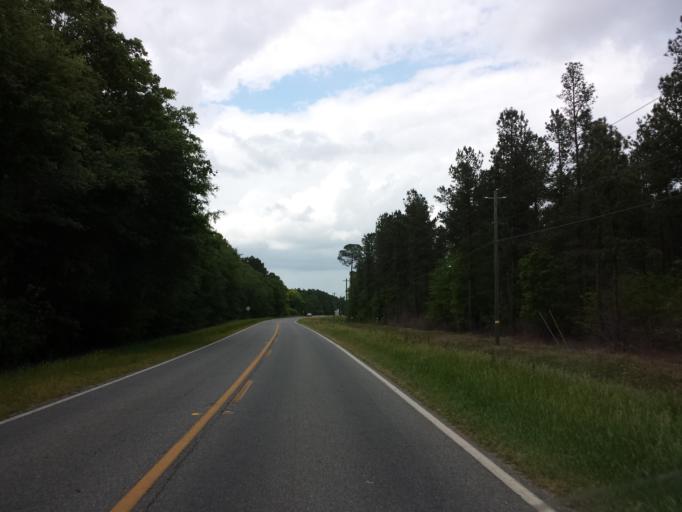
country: US
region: Georgia
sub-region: Cook County
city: Sparks
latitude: 31.2086
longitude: -83.4514
